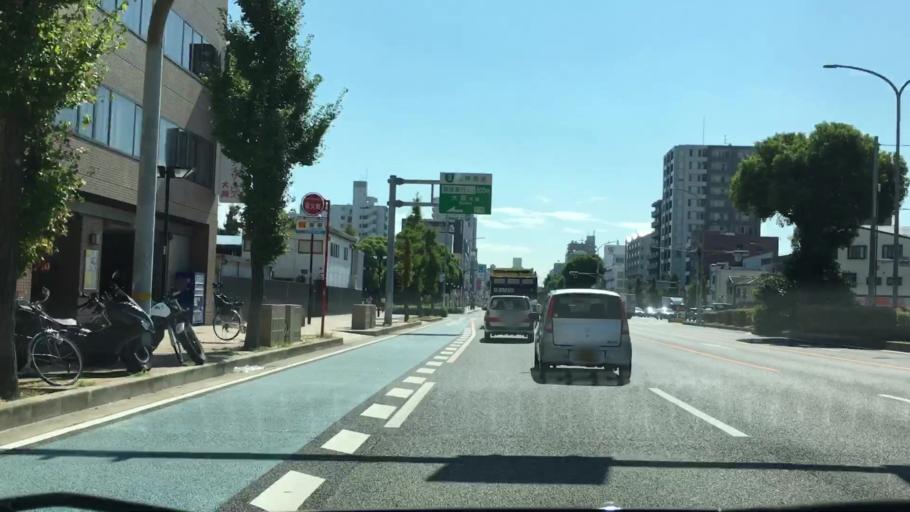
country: JP
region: Hyogo
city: Kobe
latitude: 34.6733
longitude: 135.1652
